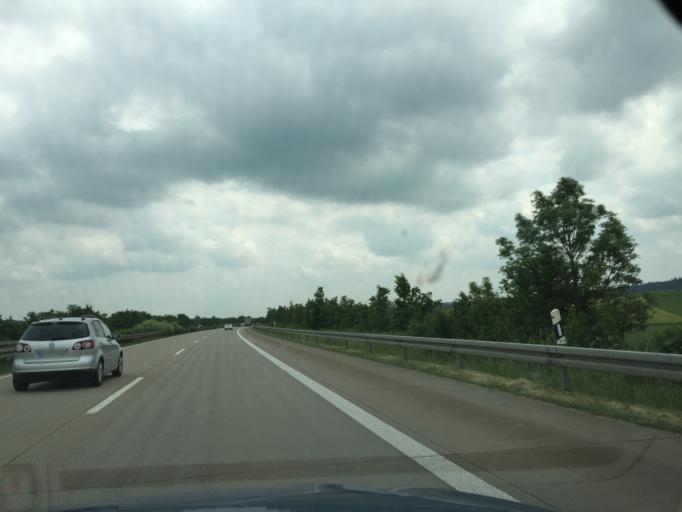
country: DE
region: Bavaria
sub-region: Regierungsbezirk Mittelfranken
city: Schopfloch
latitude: 49.1646
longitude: 10.2589
